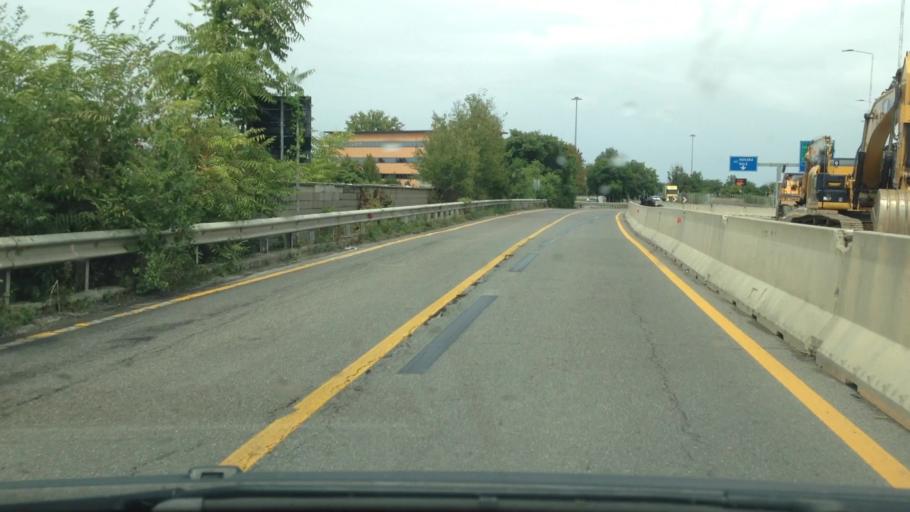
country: IT
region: Piedmont
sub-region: Provincia di Alessandria
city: Tortona
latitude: 44.9045
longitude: 8.8376
